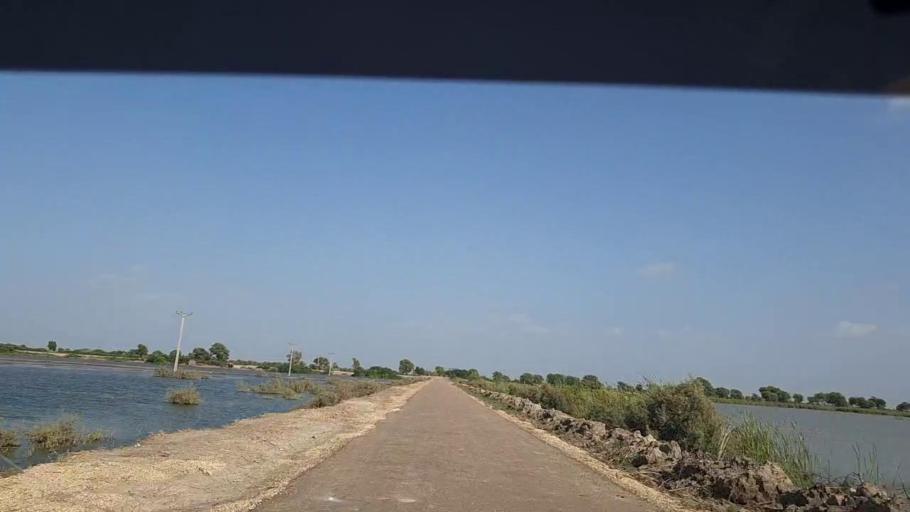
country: PK
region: Sindh
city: Kadhan
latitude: 24.4643
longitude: 68.8436
